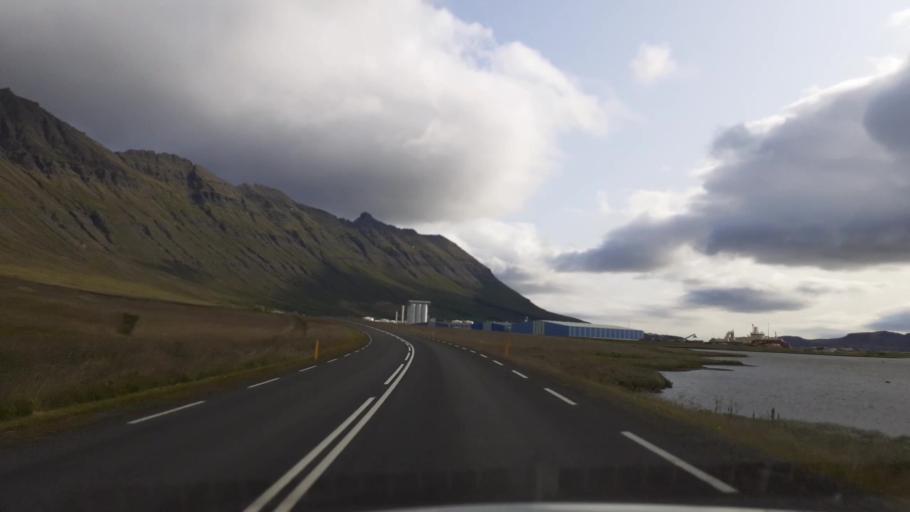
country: IS
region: East
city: Neskaupstadur
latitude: 65.1337
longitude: -13.7541
